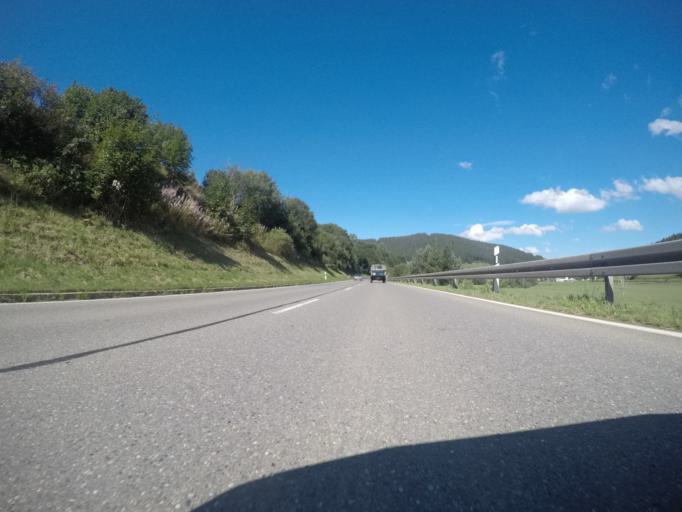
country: DE
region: Baden-Wuerttemberg
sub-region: Freiburg Region
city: Furtwangen im Schwarzwald
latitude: 48.0479
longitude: 8.2435
